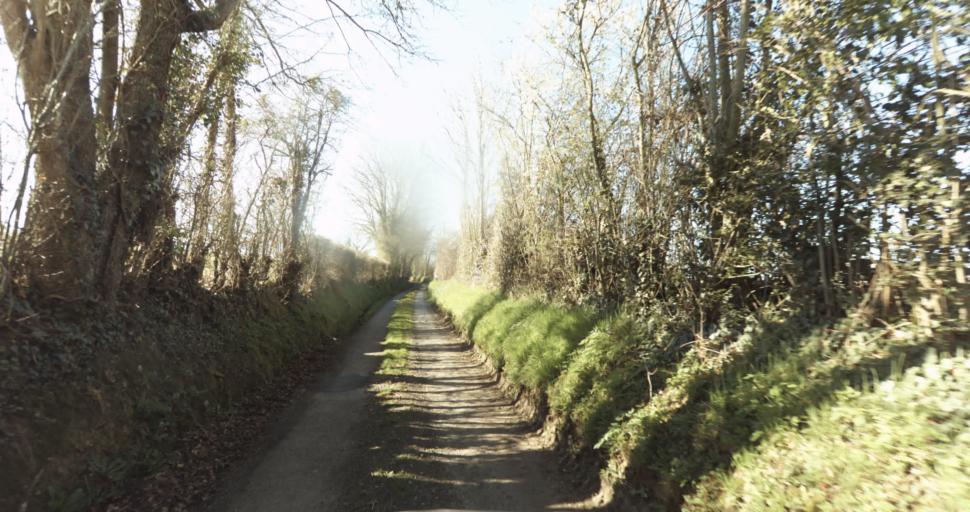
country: FR
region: Lower Normandy
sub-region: Departement du Calvados
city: Livarot
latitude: 49.0299
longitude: 0.0608
